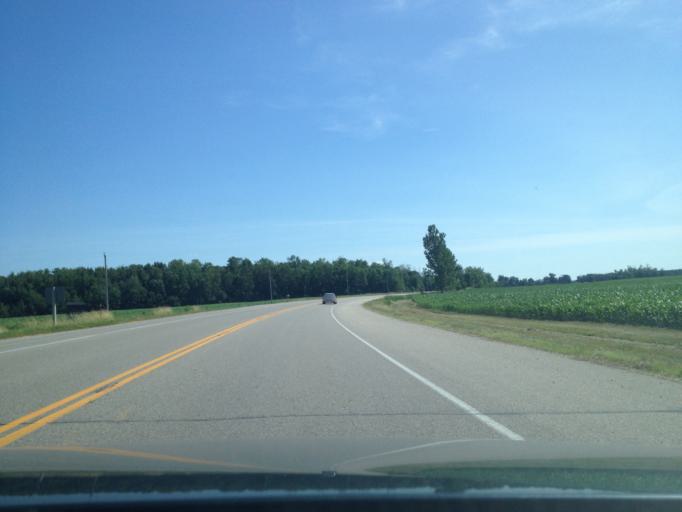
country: CA
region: Ontario
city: Stratford
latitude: 43.4988
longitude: -80.8800
